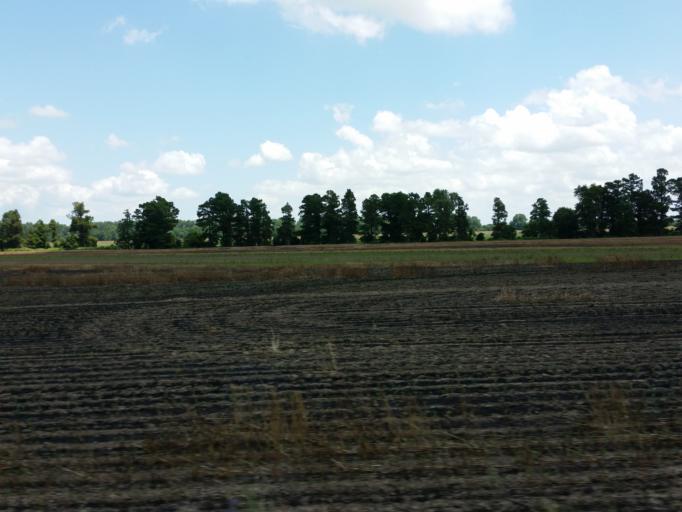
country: US
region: Kentucky
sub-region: Fulton County
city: Hickman
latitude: 36.5542
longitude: -89.2774
